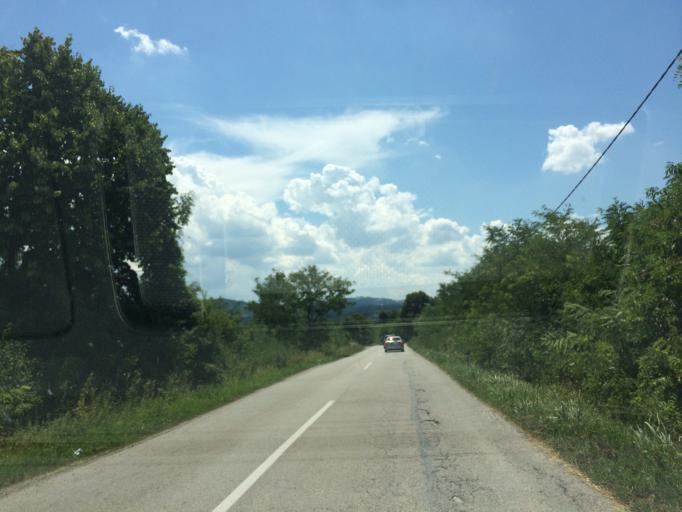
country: RS
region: Central Serbia
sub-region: Kolubarski Okrug
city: Ljig
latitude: 44.2324
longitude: 20.1820
